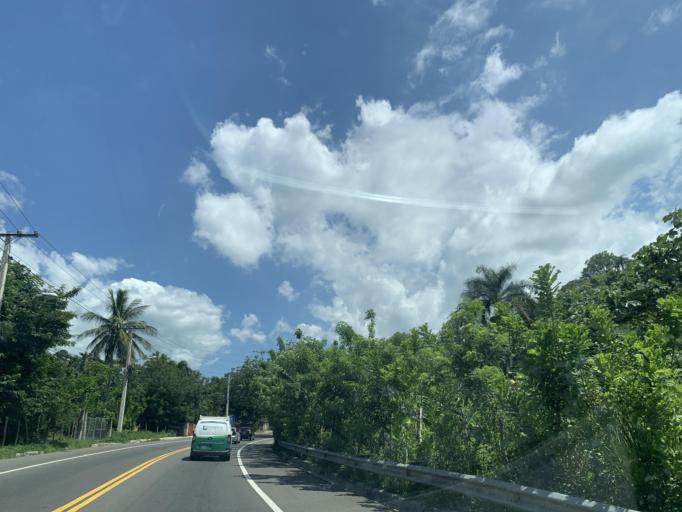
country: DO
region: Puerto Plata
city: Altamira
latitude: 19.6927
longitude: -70.8398
